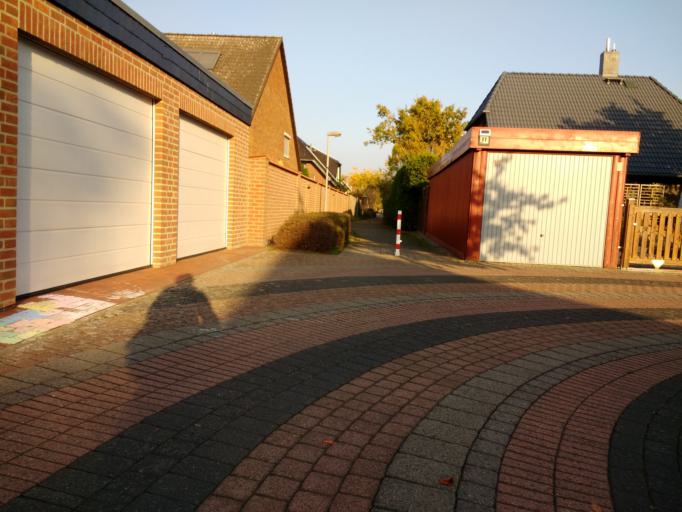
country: DE
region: Lower Saxony
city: Gifhorn
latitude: 52.4638
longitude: 10.5533
